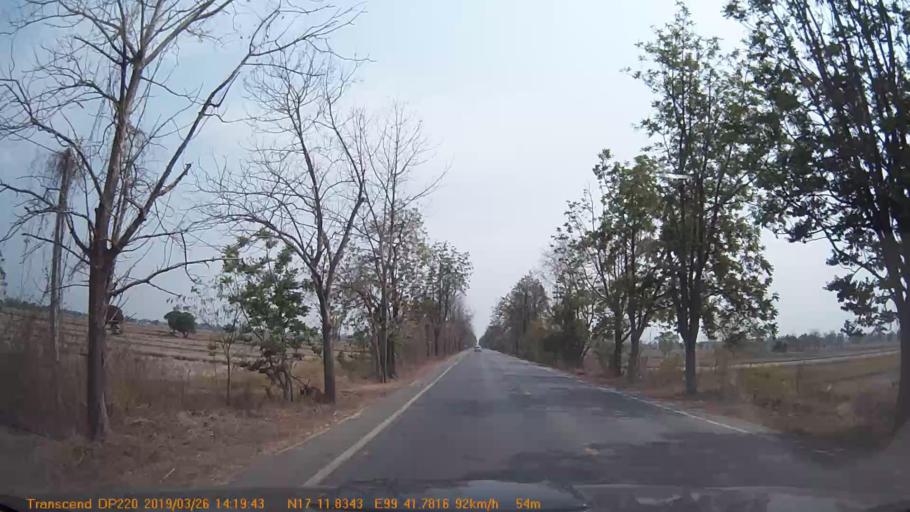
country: TH
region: Sukhothai
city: Si Samrong
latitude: 17.1969
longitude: 99.6964
